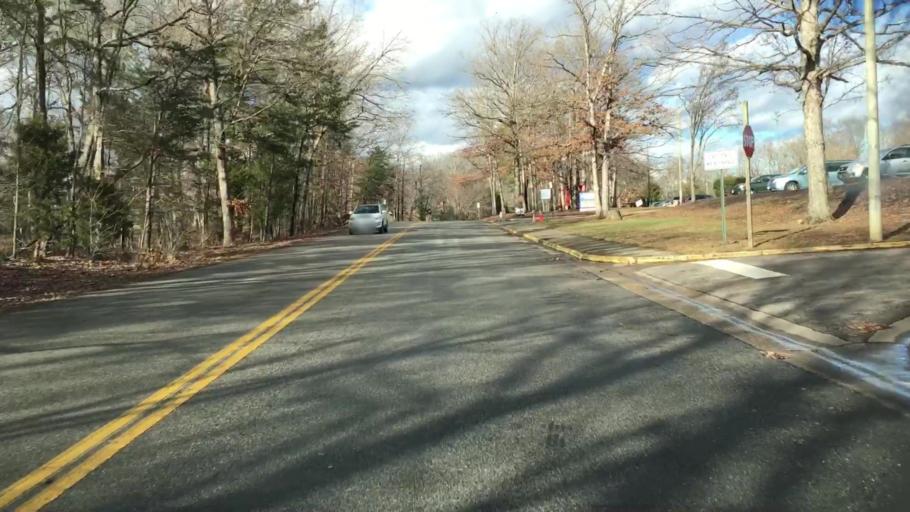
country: US
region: Virginia
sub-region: Chesterfield County
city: Bon Air
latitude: 37.5307
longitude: -77.6147
